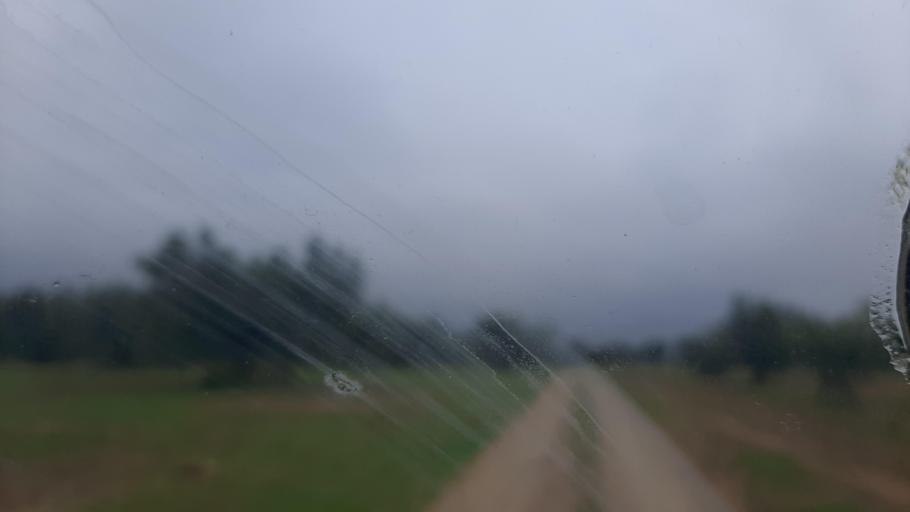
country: TN
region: Tunis
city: La Sebala du Mornag
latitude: 36.5788
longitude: 10.2904
